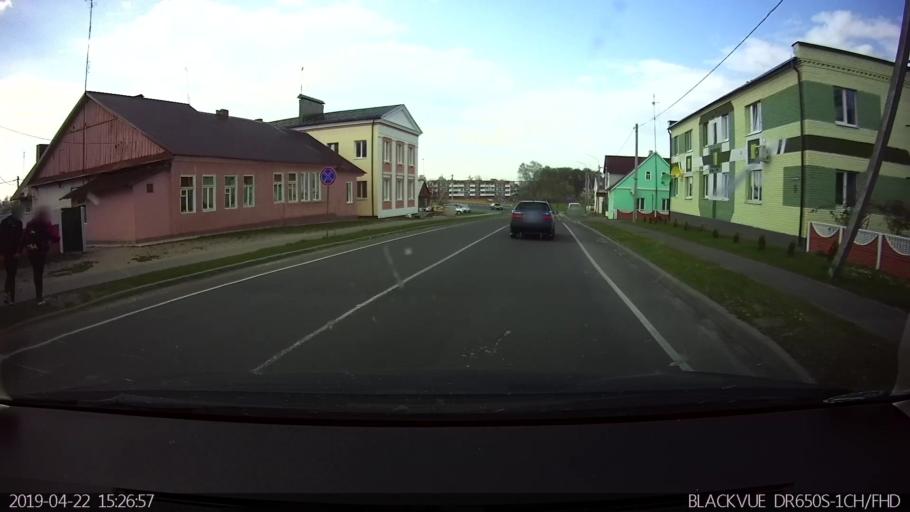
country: BY
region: Brest
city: Vysokaye
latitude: 52.3683
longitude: 23.3756
